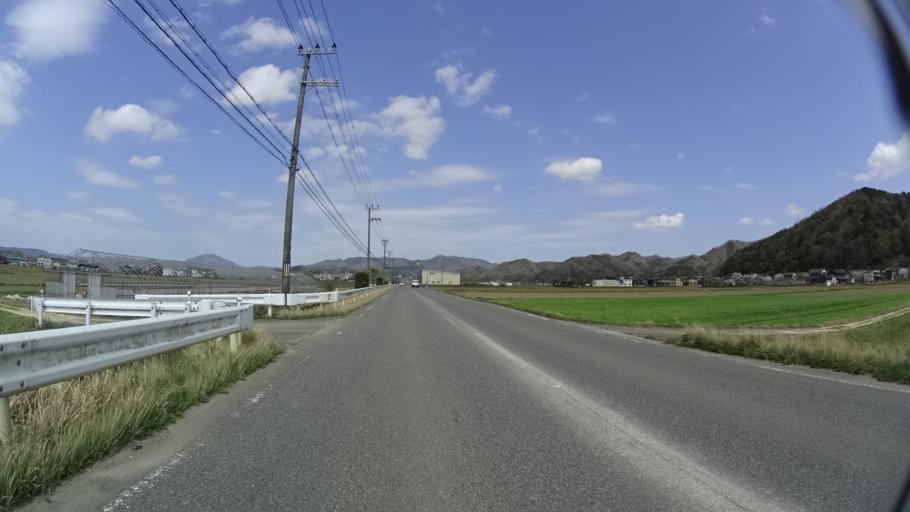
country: JP
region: Hyogo
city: Toyooka
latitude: 35.5212
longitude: 134.8399
